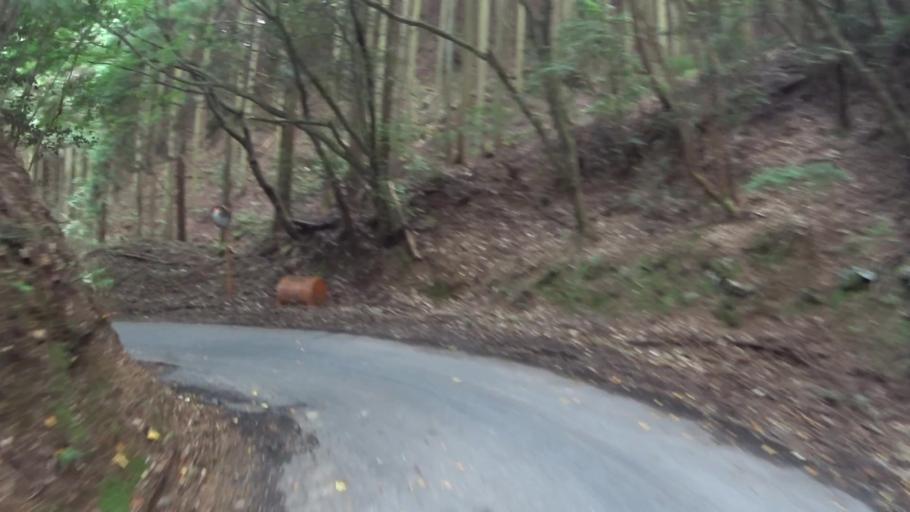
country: JP
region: Shiga Prefecture
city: Otsu-shi
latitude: 34.9508
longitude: 135.8390
